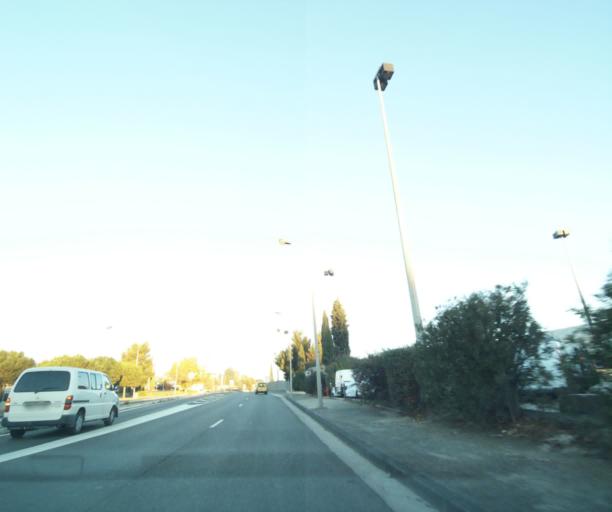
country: FR
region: Provence-Alpes-Cote d'Azur
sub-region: Departement des Bouches-du-Rhone
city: La Penne-sur-Huveaune
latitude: 43.2936
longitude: 5.4837
